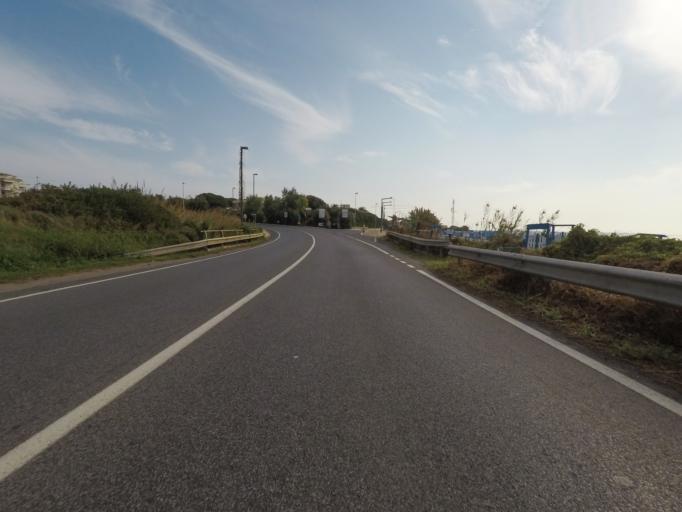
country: IT
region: Latium
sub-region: Citta metropolitana di Roma Capitale
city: Santa Marinella
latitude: 42.0361
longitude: 11.8331
